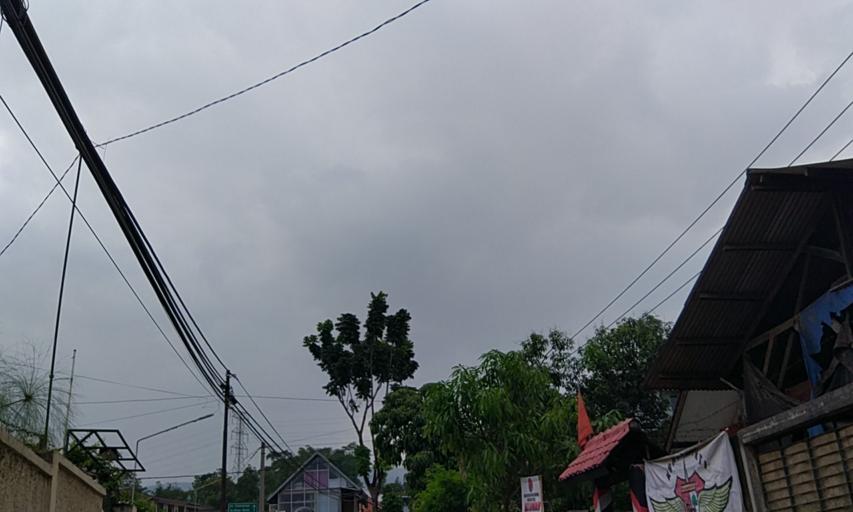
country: ID
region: West Java
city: Bandung
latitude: -6.8916
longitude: 107.6846
